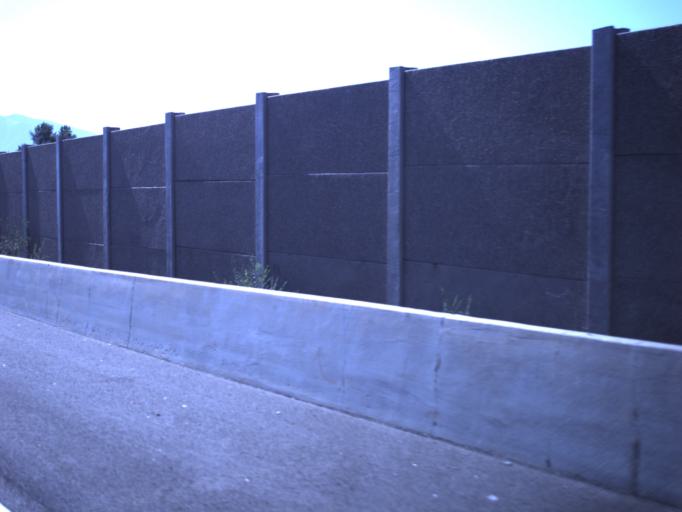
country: US
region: Utah
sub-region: Salt Lake County
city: Taylorsville
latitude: 40.6435
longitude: -111.9282
